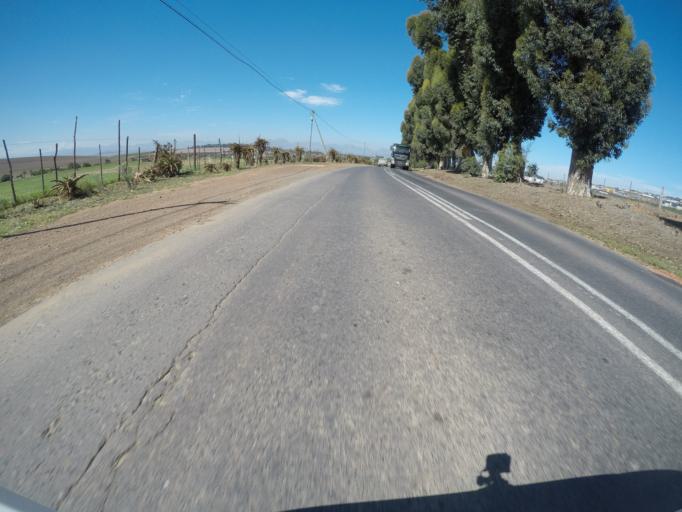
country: ZA
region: Western Cape
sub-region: City of Cape Town
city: Kraaifontein
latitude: -33.8114
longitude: 18.6280
